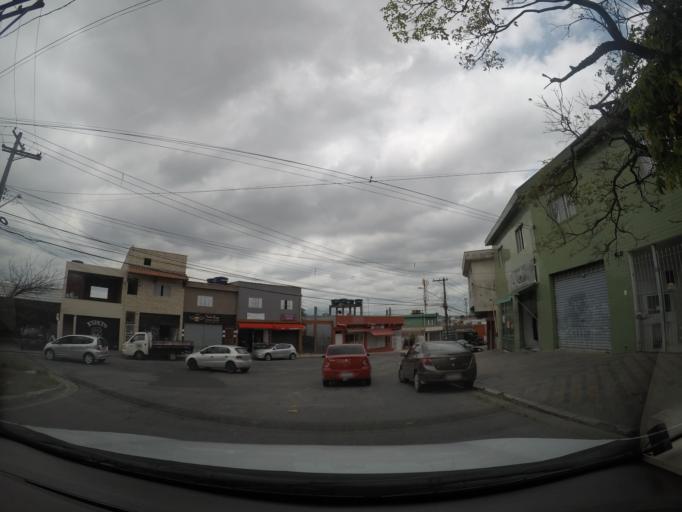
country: BR
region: Sao Paulo
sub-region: Itaquaquecetuba
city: Itaquaquecetuba
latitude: -23.4296
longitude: -46.4341
